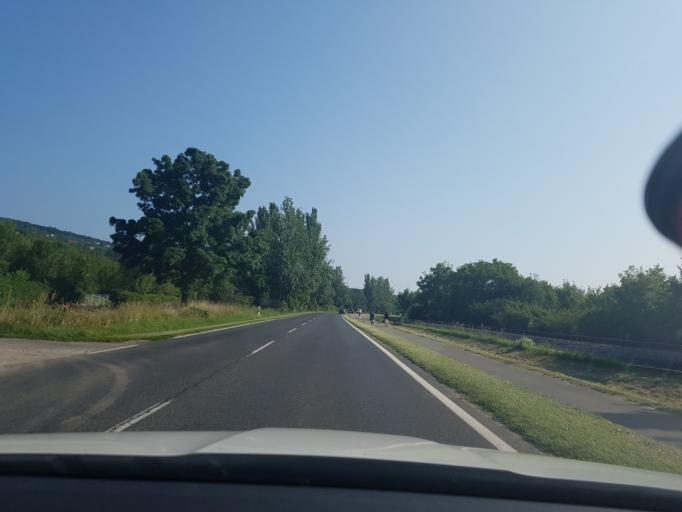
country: HU
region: Veszprem
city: Balatonalmadi
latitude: 46.9917
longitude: 17.9871
